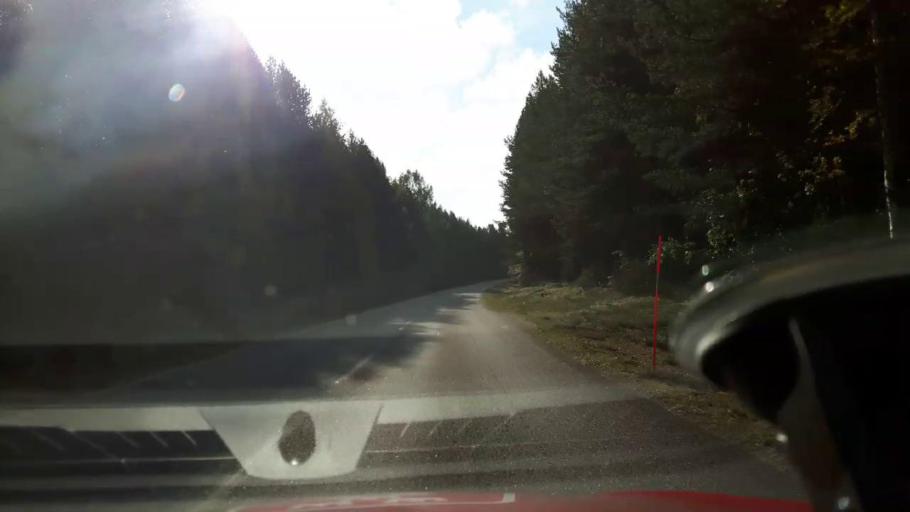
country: SE
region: Vaesternorrland
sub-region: Ange Kommun
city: Ange
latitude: 62.0903
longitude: 15.0918
